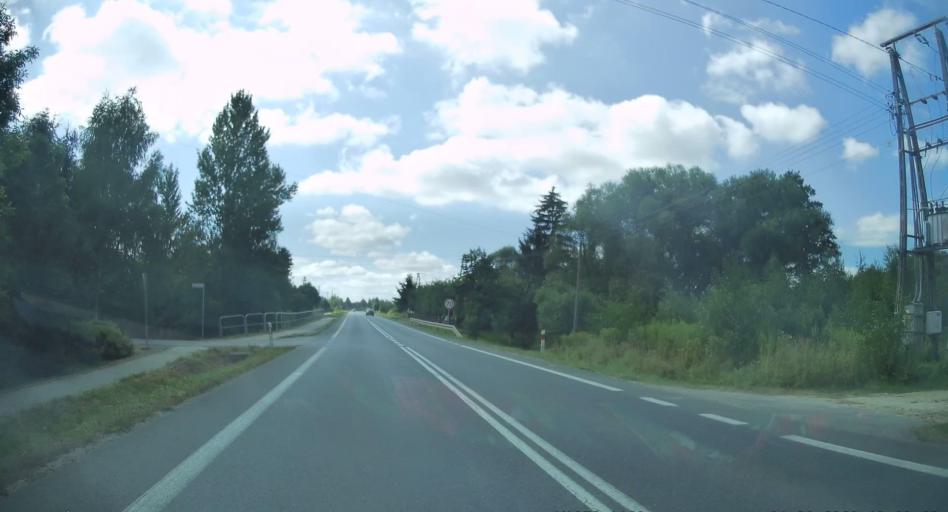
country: PL
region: Subcarpathian Voivodeship
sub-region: Powiat mielecki
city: Przeclaw
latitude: 50.1762
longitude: 21.4937
